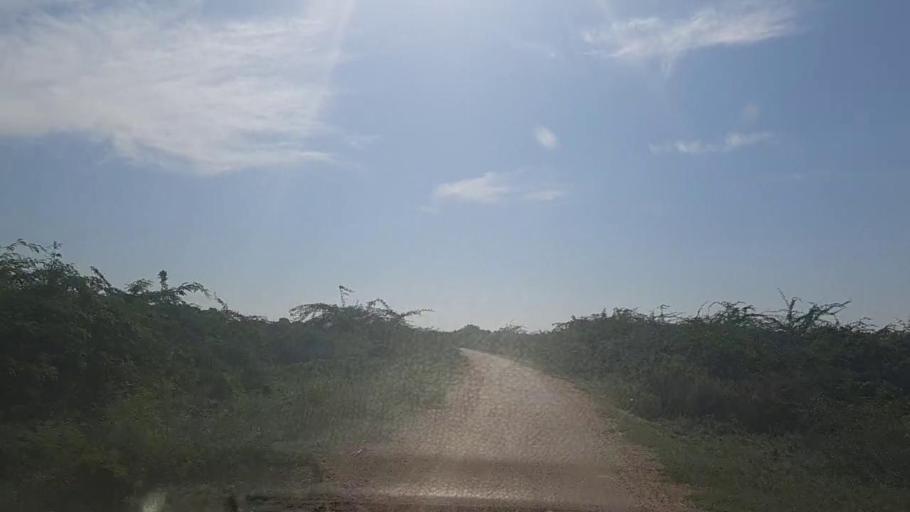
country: PK
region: Sindh
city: Mirpur Batoro
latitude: 24.6683
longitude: 68.1837
